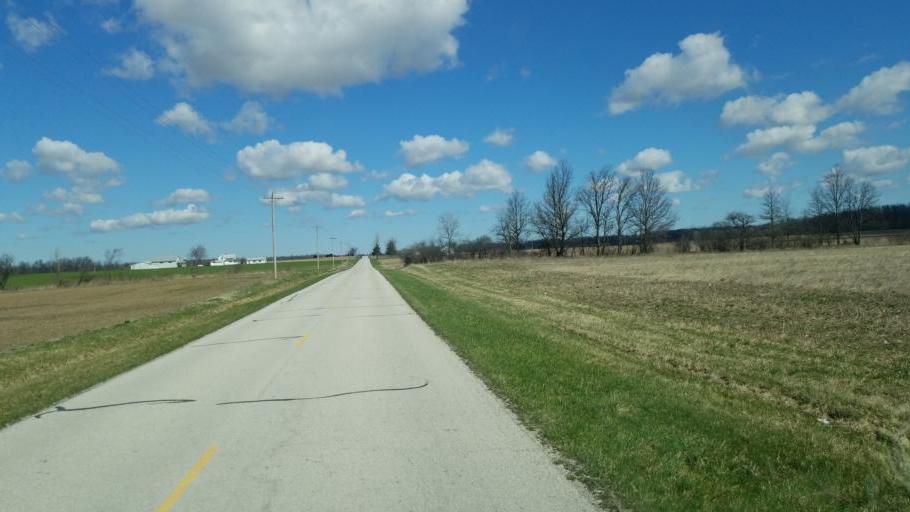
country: US
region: Ohio
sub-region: Sandusky County
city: Mount Carmel
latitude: 41.1347
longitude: -82.9384
